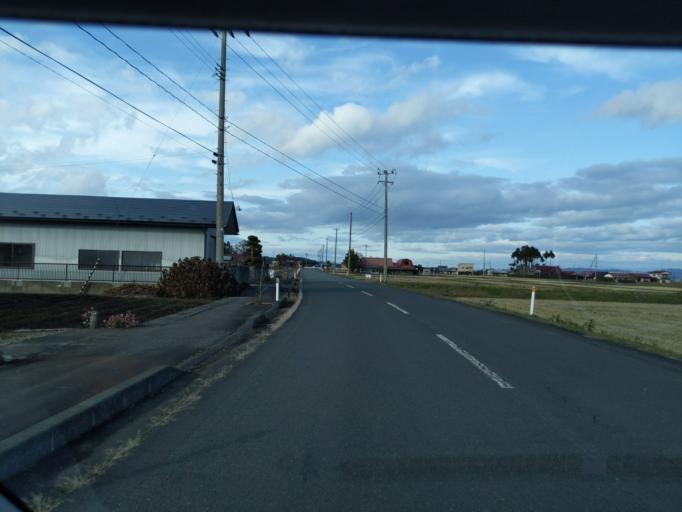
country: JP
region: Iwate
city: Mizusawa
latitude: 39.1443
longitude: 141.0893
